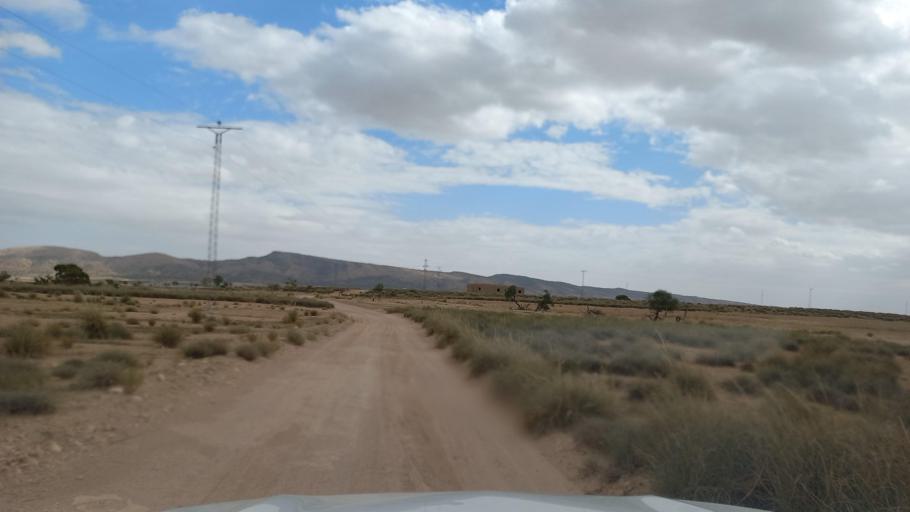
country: TN
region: Al Qasrayn
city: Sbiba
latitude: 35.3816
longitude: 9.1159
